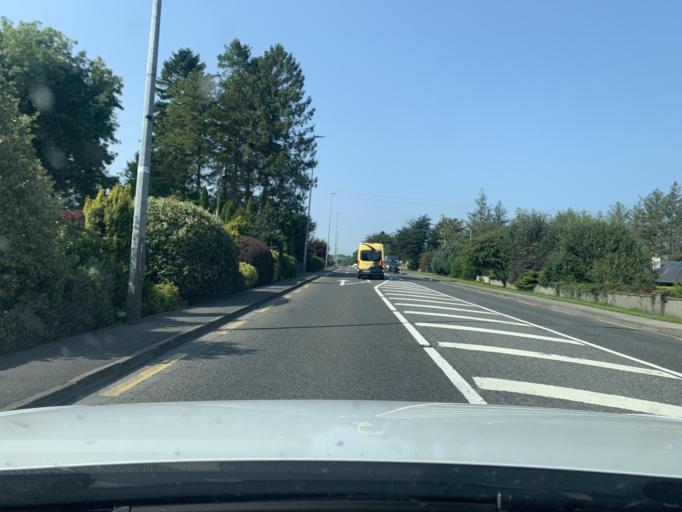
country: IE
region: Leinster
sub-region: An Iarmhi
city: Athlone
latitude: 53.4567
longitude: -7.9967
